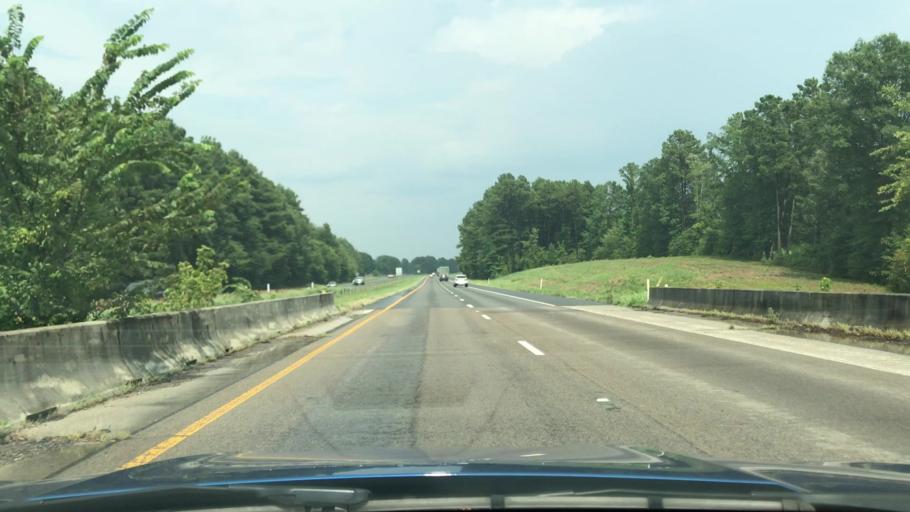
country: US
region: Texas
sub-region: Harrison County
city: Hallsville
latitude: 32.4827
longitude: -94.5320
